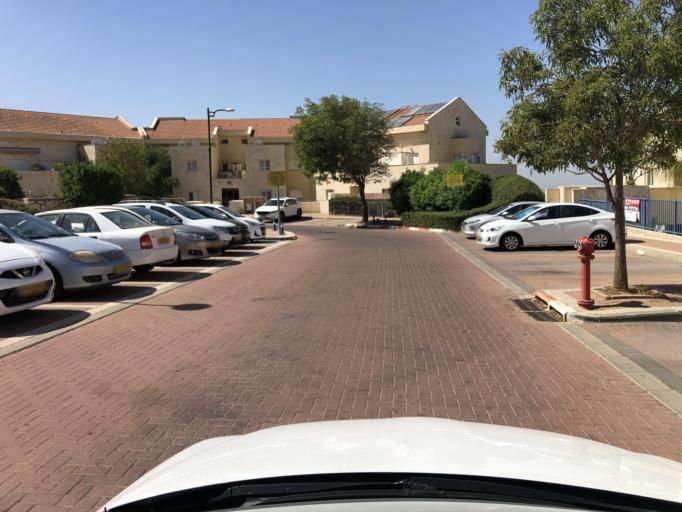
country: PS
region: West Bank
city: An Nabi Ilyas
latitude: 32.1671
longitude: 35.0197
